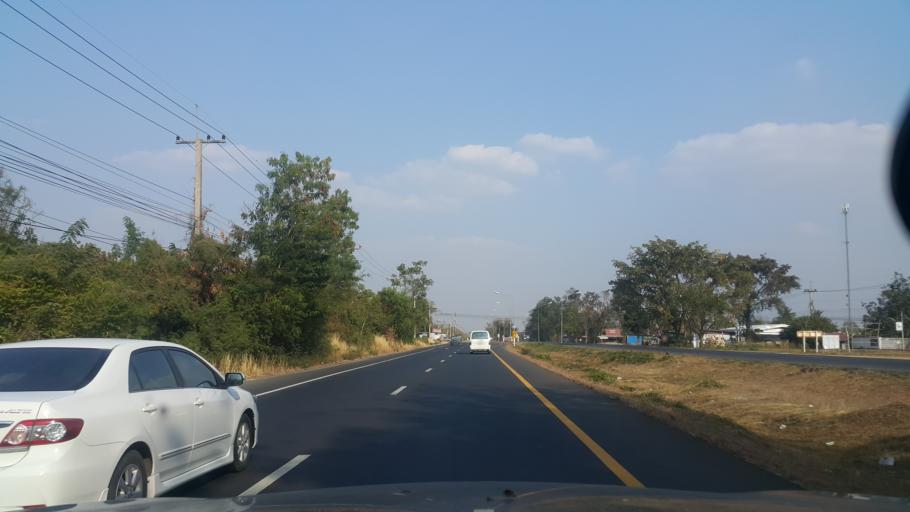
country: TH
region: Buriram
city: Nang Rong
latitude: 14.6340
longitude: 102.7321
